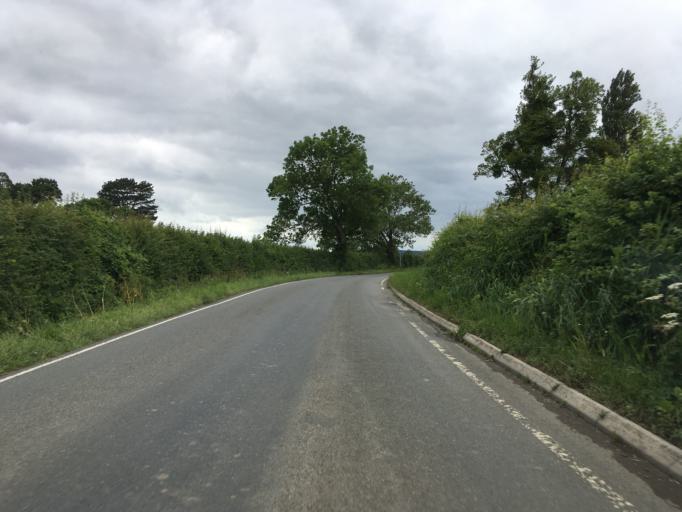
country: GB
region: England
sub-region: Gloucestershire
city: Stonehouse
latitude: 51.7772
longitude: -2.3753
